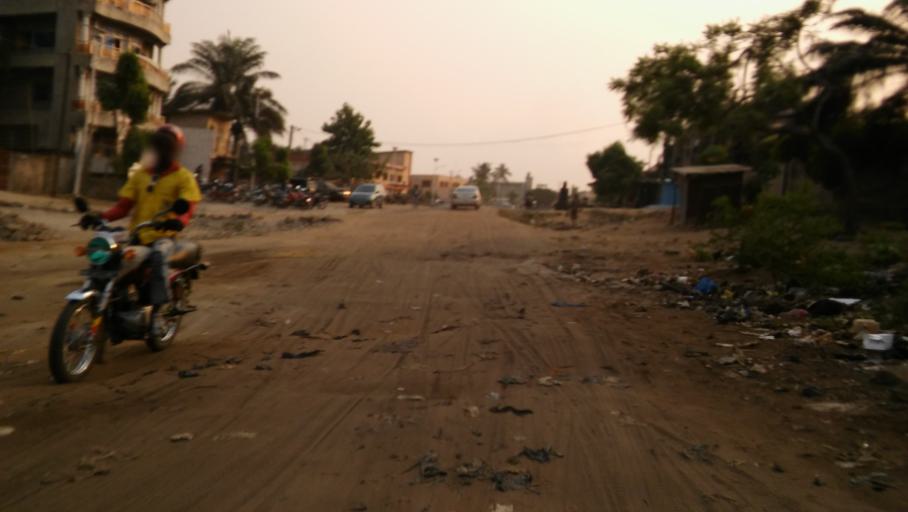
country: BJ
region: Littoral
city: Cotonou
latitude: 6.3903
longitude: 2.3775
